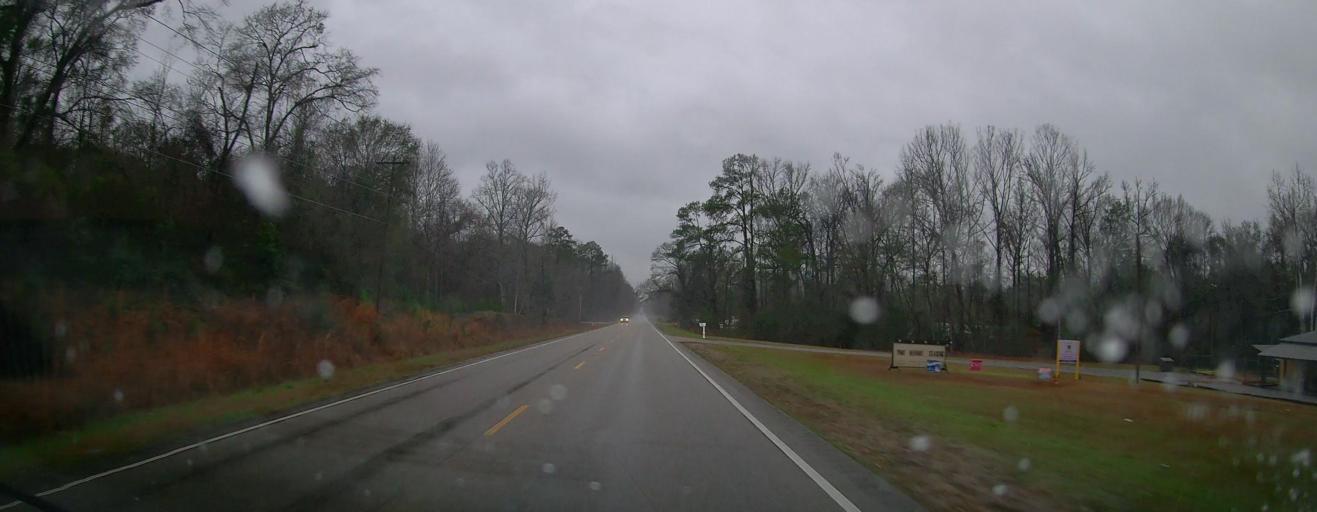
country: US
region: Alabama
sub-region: Autauga County
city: Prattville
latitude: 32.4798
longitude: -86.5294
